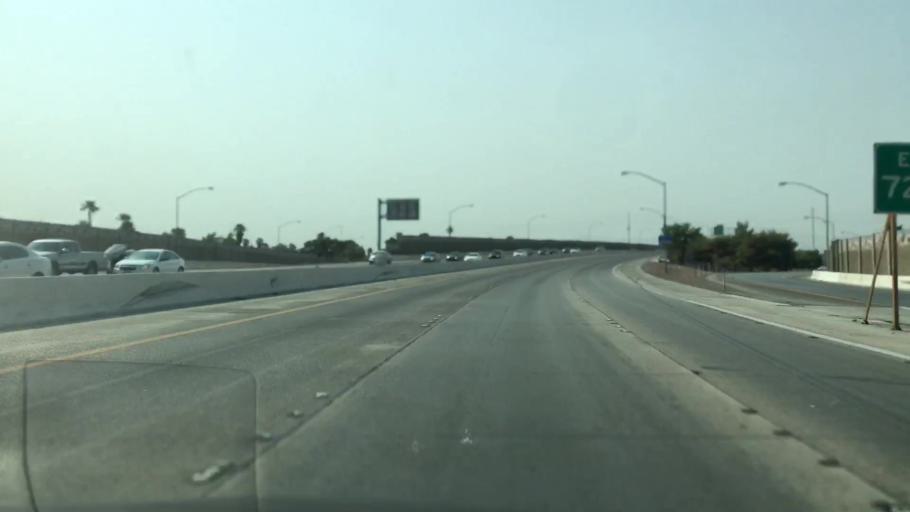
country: US
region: Nevada
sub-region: Clark County
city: Winchester
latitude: 36.1631
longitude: -115.0923
